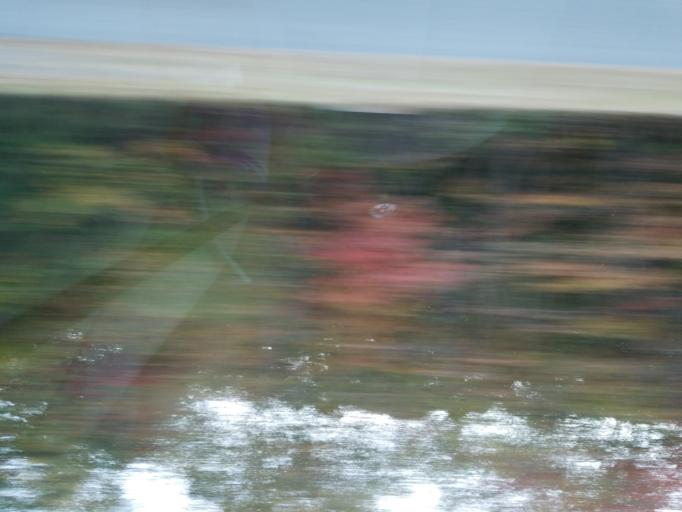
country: US
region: Georgia
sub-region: Forsyth County
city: Cumming
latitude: 34.2873
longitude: -84.0755
